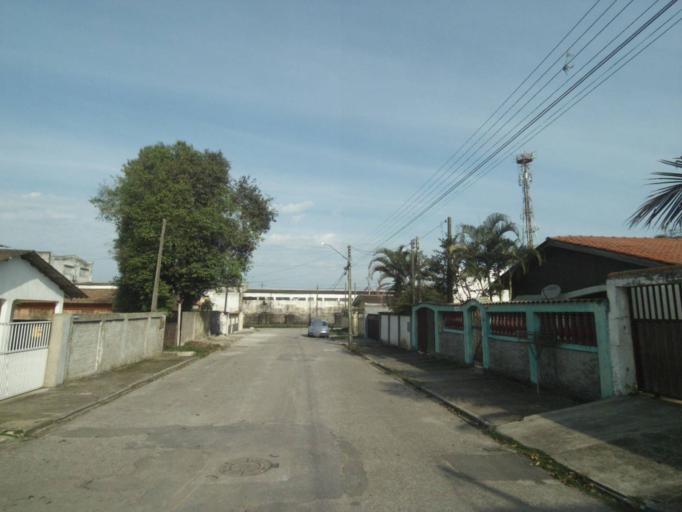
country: BR
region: Parana
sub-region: Paranagua
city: Paranagua
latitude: -25.5374
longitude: -48.5339
